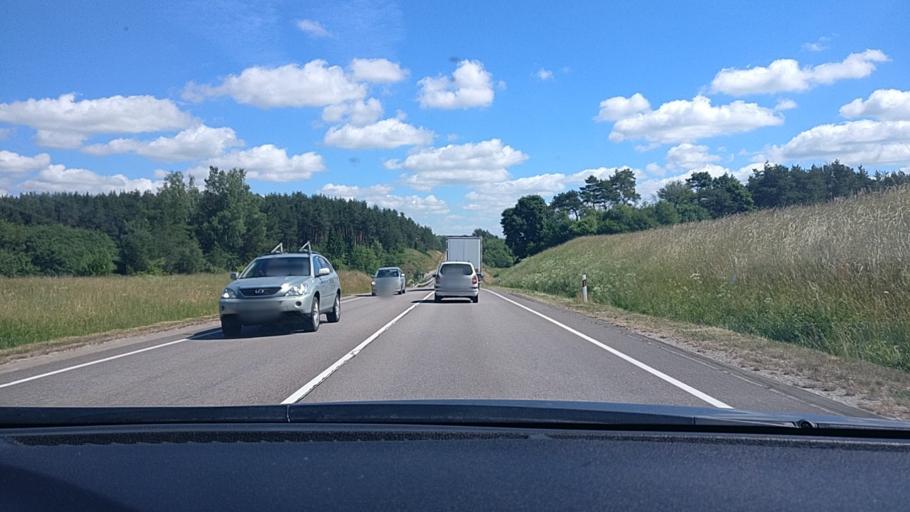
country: LT
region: Vilnius County
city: Ukmerge
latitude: 55.2897
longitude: 24.8409
